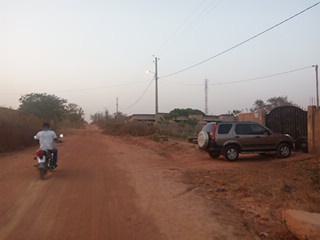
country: BJ
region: Borgou
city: Parakou
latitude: 9.3188
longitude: 2.5988
